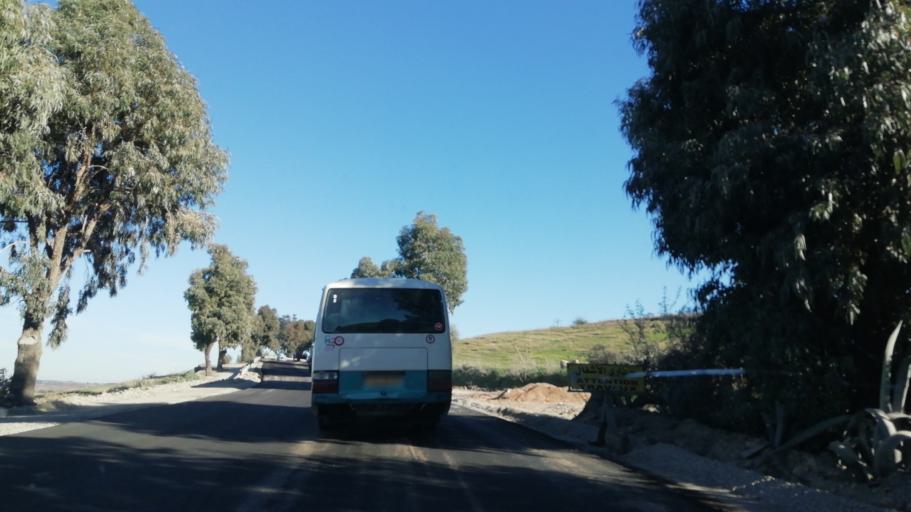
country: DZ
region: Relizane
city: Smala
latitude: 35.6606
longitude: 0.8136
